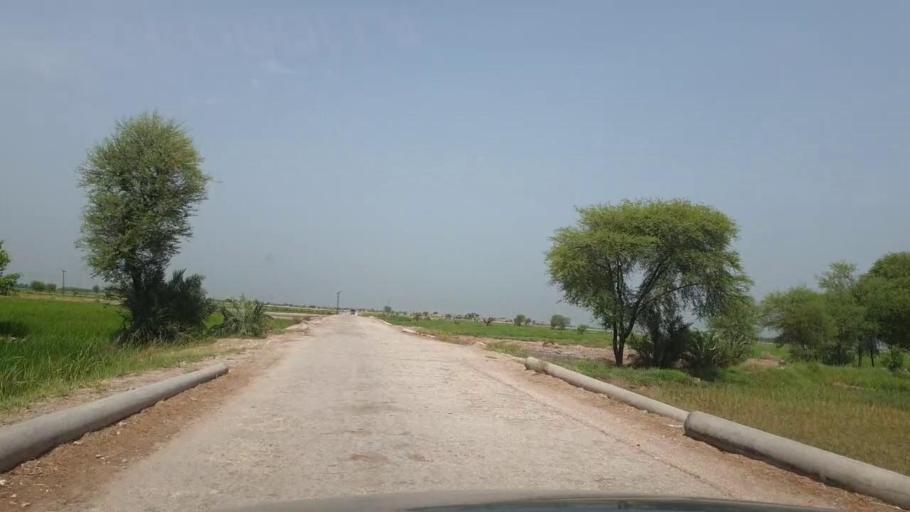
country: PK
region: Sindh
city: Garhi Yasin
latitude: 27.8534
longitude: 68.4388
